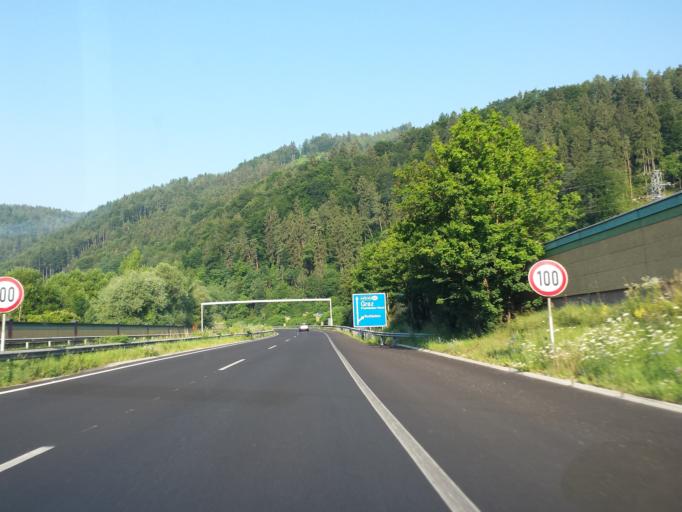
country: AT
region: Styria
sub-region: Politischer Bezirk Graz-Umgebung
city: Frohnleiten
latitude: 47.2896
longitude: 15.3139
